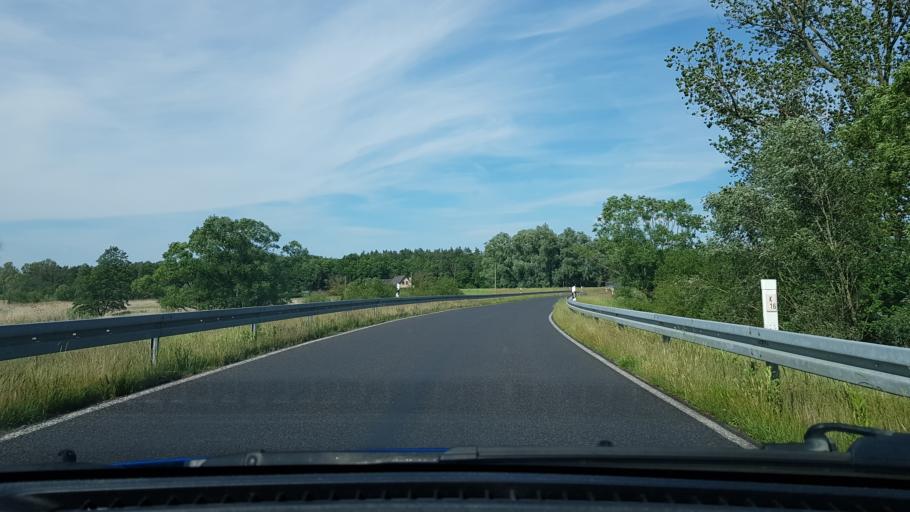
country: DE
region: Mecklenburg-Vorpommern
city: Boizenburg
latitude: 53.3576
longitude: 10.8265
